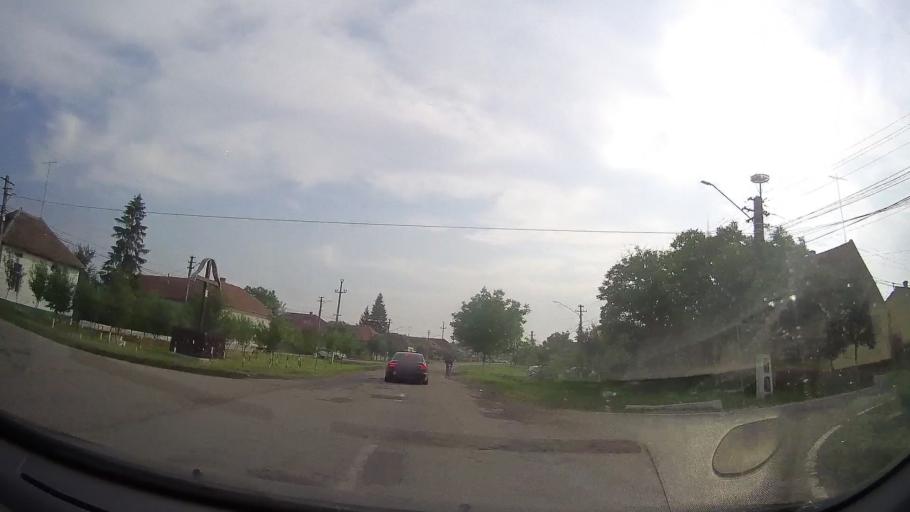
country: RO
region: Timis
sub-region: Comuna Peciu Nou
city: Peciu Nou
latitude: 45.5991
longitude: 21.0501
